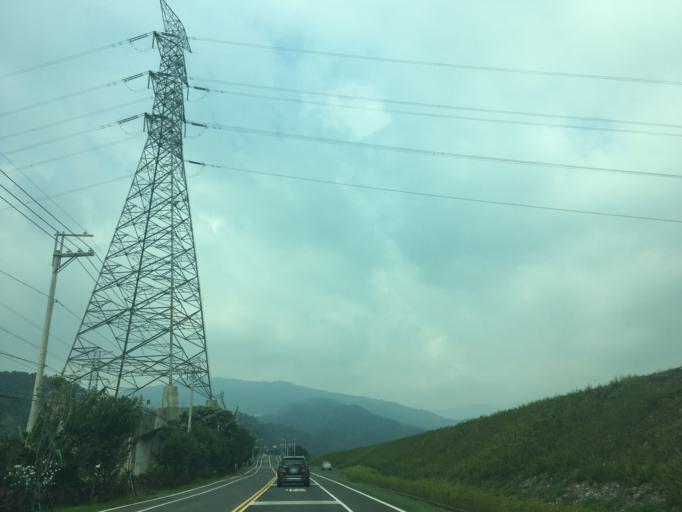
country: TW
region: Taiwan
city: Fengyuan
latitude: 24.2922
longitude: 120.8648
